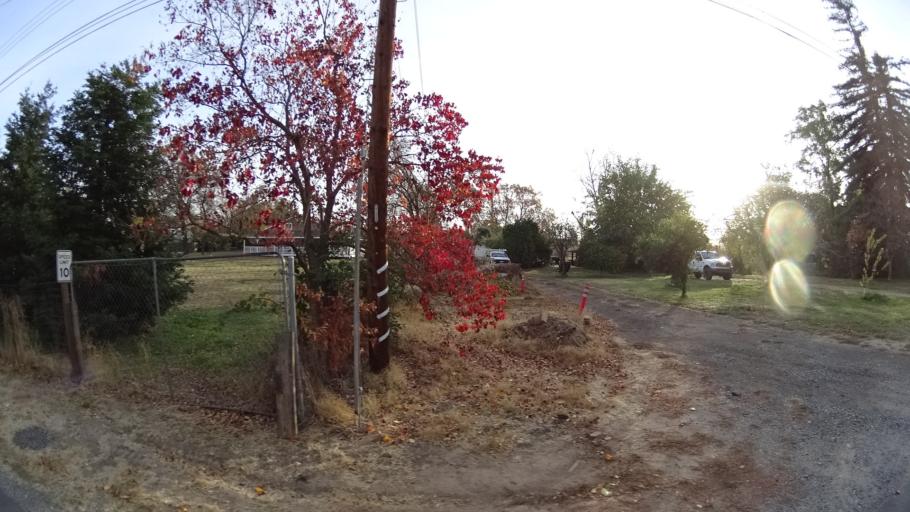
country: US
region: California
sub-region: Sacramento County
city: Citrus Heights
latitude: 38.7212
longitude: -121.2755
